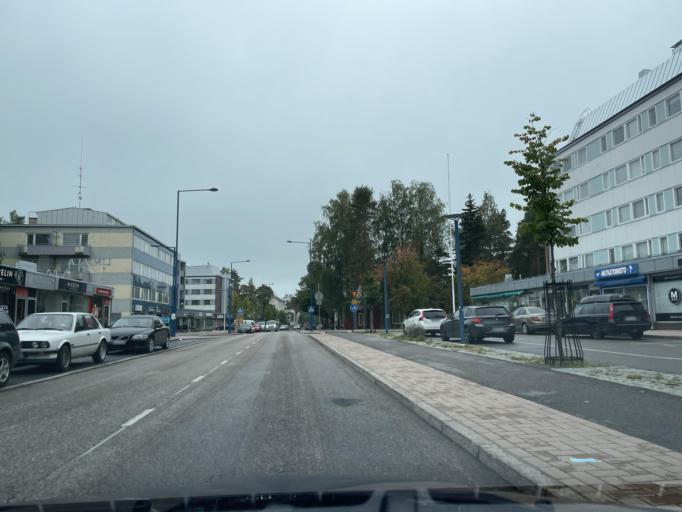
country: FI
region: Uusimaa
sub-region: Helsinki
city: Hyvinge
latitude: 60.6287
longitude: 24.8569
